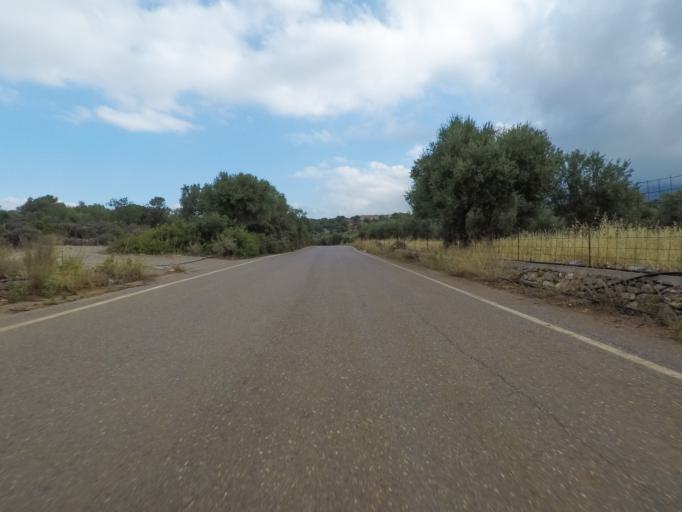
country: GR
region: Crete
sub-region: Nomos Lasithiou
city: Kritsa
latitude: 35.1721
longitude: 25.6535
